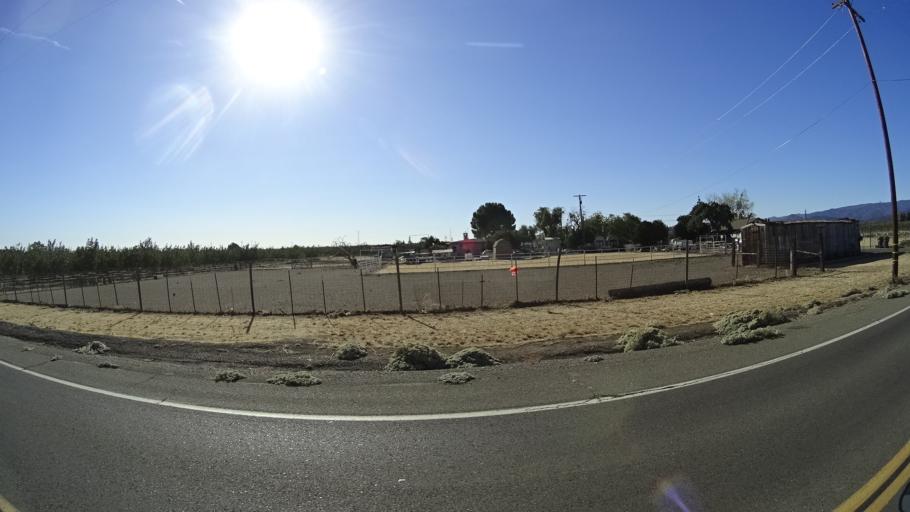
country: US
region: California
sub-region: Yolo County
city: Winters
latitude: 38.5128
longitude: -122.0044
